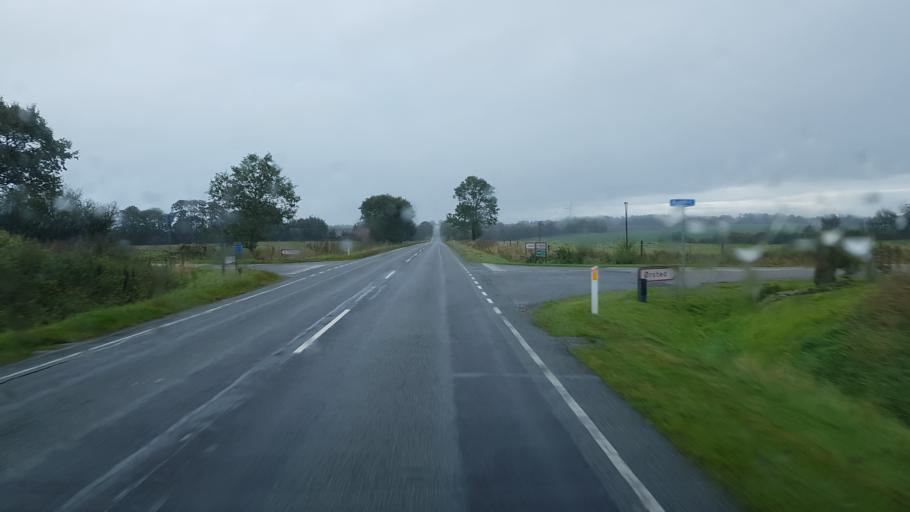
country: DK
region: South Denmark
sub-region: Kolding Kommune
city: Vamdrup
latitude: 55.3473
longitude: 9.2536
